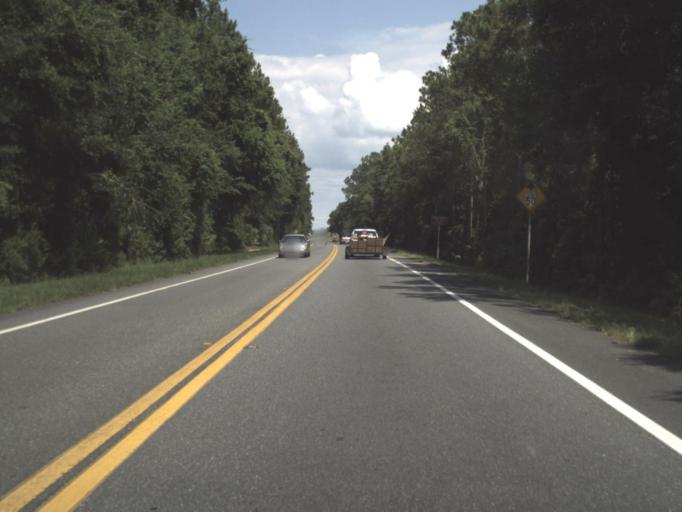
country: US
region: Florida
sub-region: Putnam County
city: Palatka
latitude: 29.6682
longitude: -81.6985
